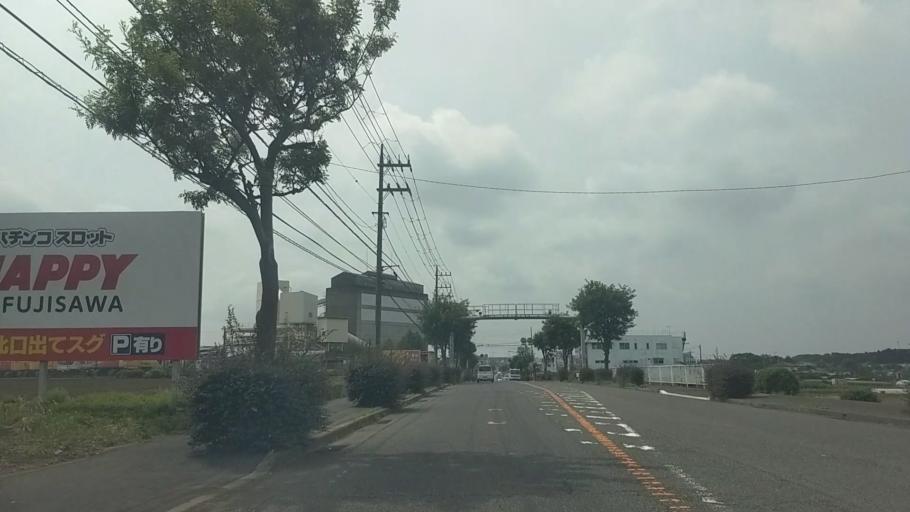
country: JP
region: Kanagawa
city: Fujisawa
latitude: 35.3770
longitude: 139.4771
